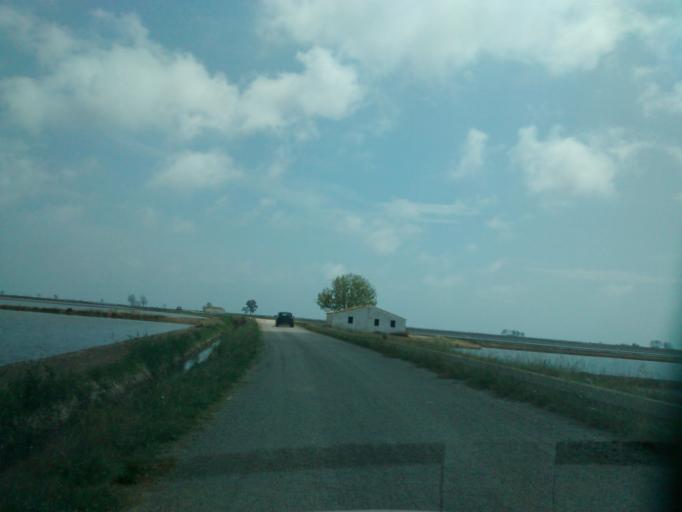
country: ES
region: Catalonia
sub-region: Provincia de Tarragona
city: Deltebre
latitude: 40.6848
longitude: 0.7879
